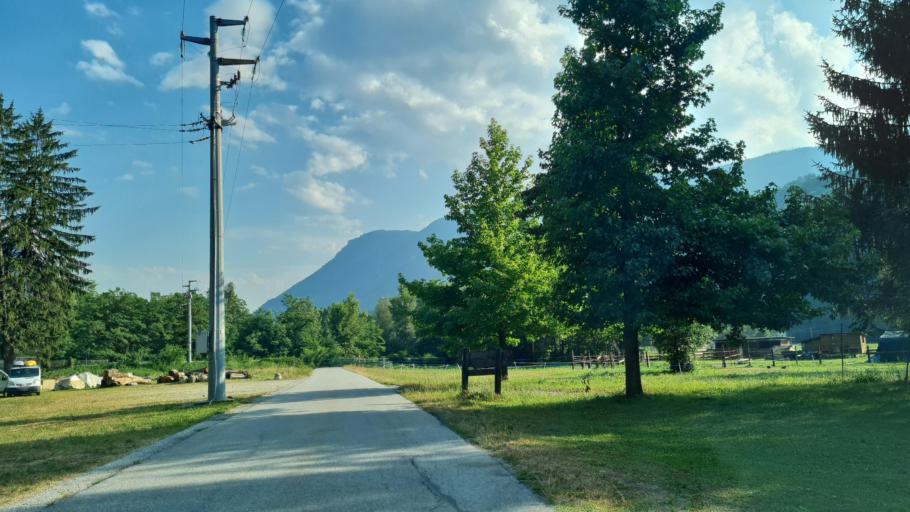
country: IT
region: Piedmont
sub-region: Provincia Verbano-Cusio-Ossola
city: Baceno
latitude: 46.2473
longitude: 8.3308
